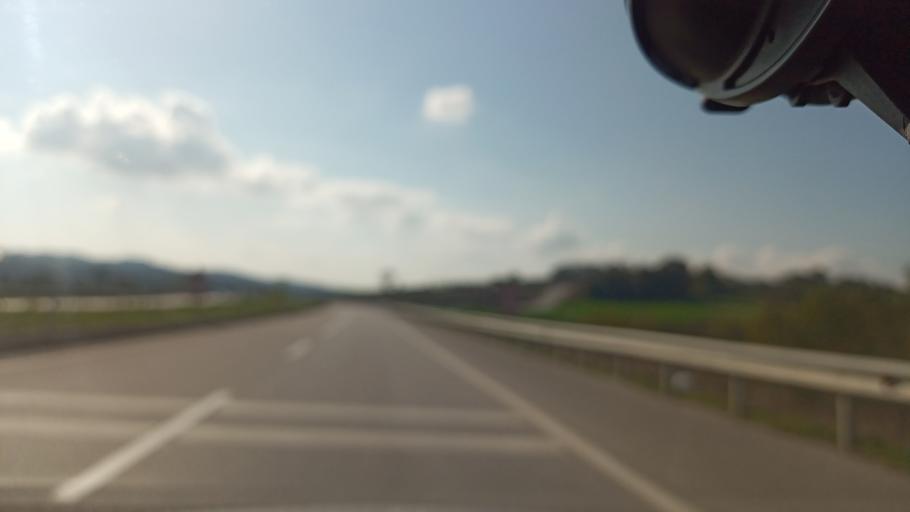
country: TR
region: Sakarya
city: Kaynarca
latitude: 41.0514
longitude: 30.3445
